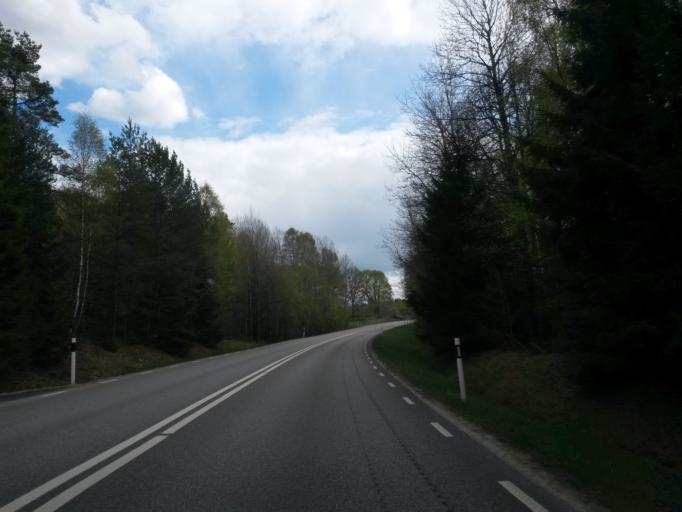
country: SE
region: Vaestra Goetaland
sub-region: Vargarda Kommun
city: Vargarda
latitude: 57.9410
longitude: 12.8478
